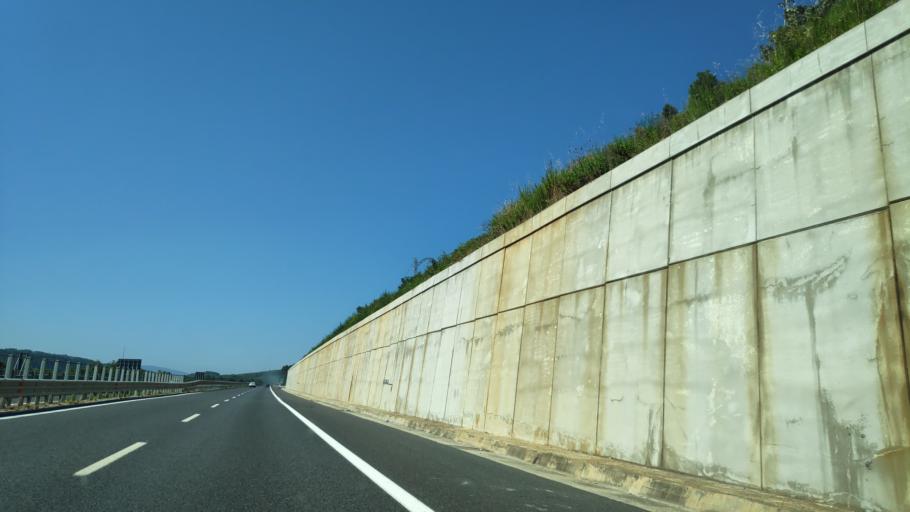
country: IT
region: Calabria
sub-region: Provincia di Reggio Calabria
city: Seminara
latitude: 38.3417
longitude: 15.8671
